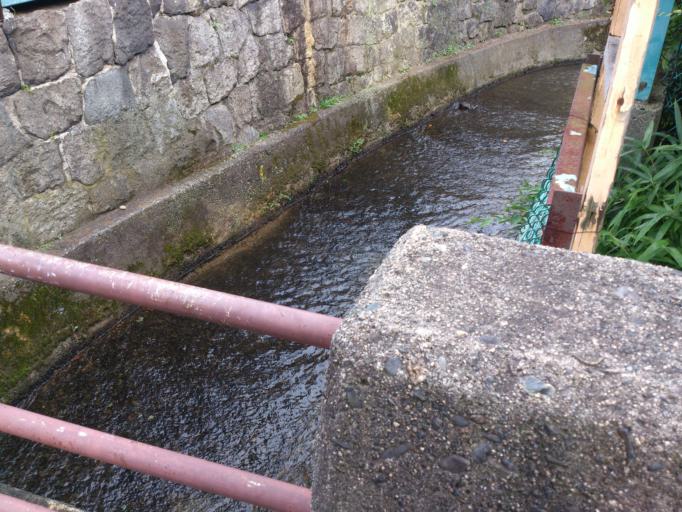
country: JP
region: Shiga Prefecture
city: Otsu-shi
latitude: 35.0056
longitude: 135.8703
